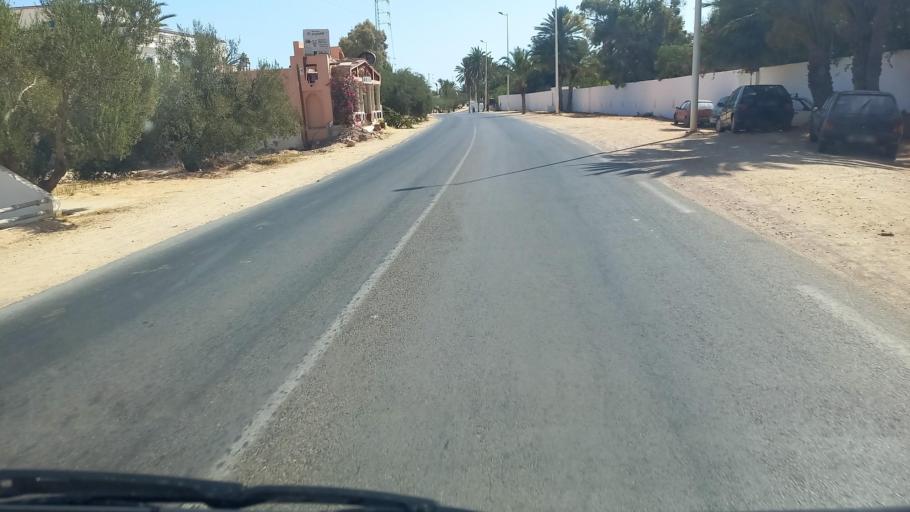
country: TN
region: Madanin
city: Midoun
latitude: 33.7810
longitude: 11.0464
